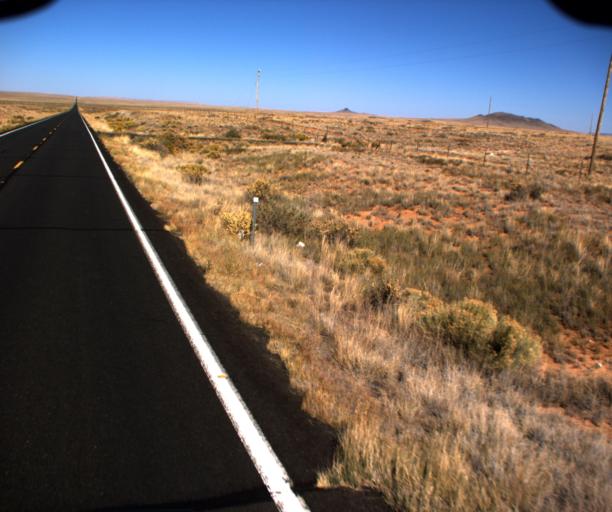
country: US
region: Arizona
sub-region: Navajo County
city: Dilkon
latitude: 35.5602
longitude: -110.4563
